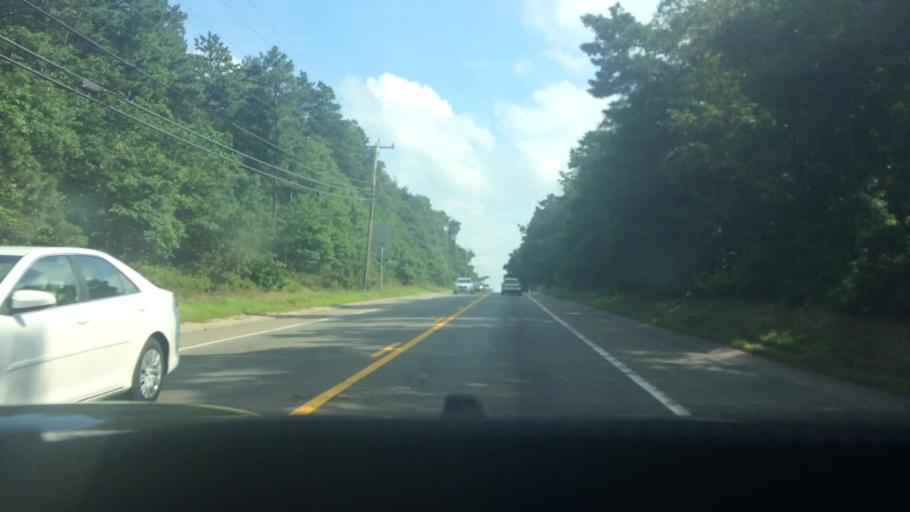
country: US
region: Massachusetts
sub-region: Barnstable County
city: Sandwich
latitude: 41.7357
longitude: -70.4919
